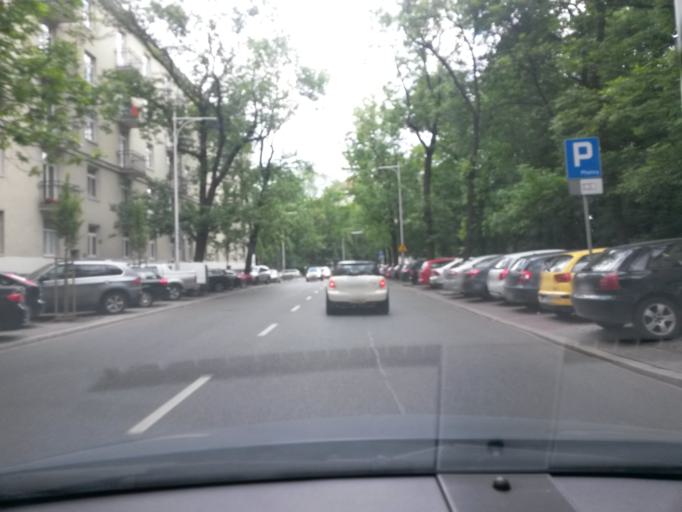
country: PL
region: Masovian Voivodeship
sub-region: Warszawa
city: Srodmiescie
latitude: 52.2278
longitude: 21.0331
